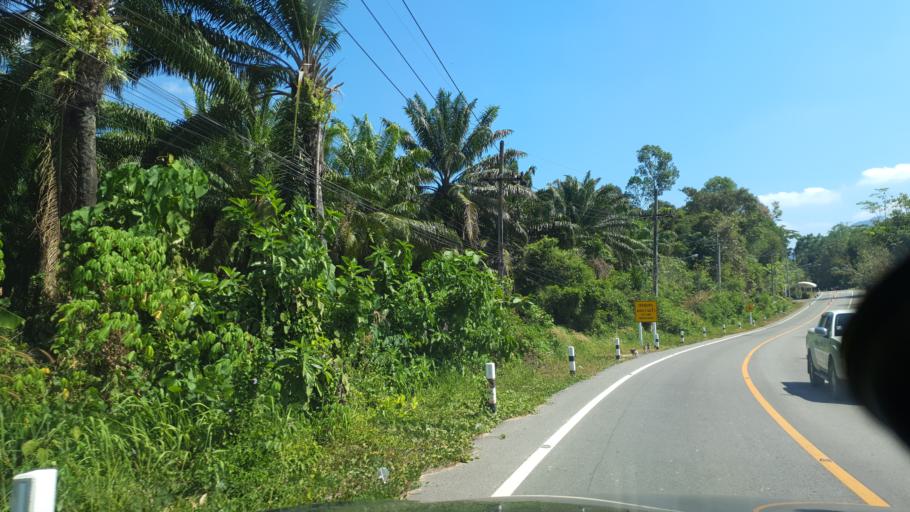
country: TH
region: Krabi
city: Khlong Thom
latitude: 7.9215
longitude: 99.2491
